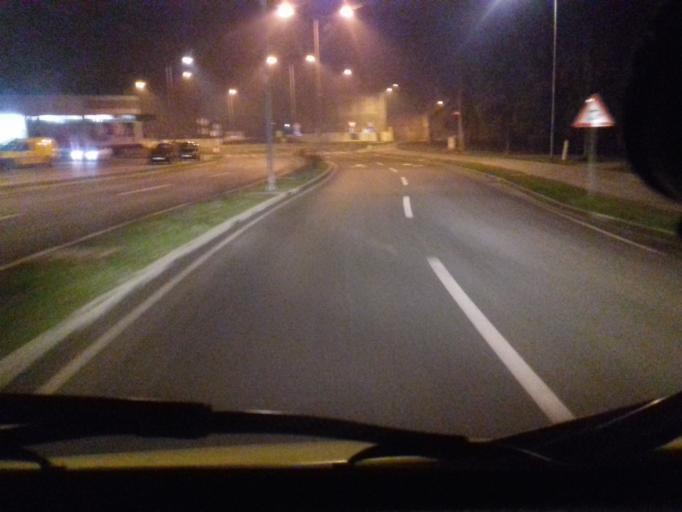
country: BA
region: Federation of Bosnia and Herzegovina
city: Zenica
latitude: 44.2036
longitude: 17.9030
